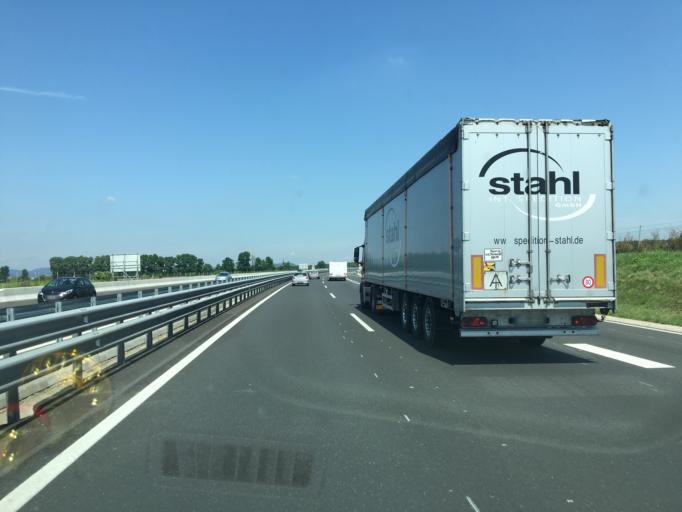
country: SI
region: Hoce-Slivnica
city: Rogoza
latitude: 46.5040
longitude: 15.6693
